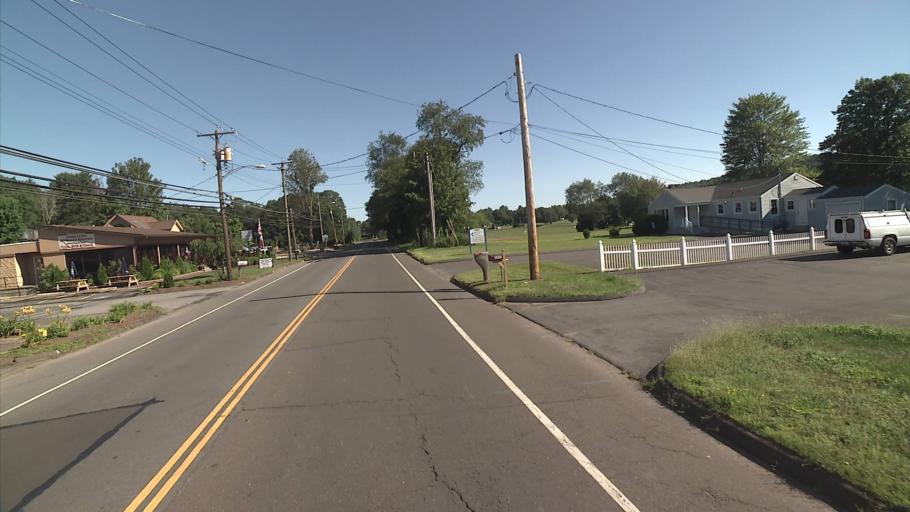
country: US
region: Connecticut
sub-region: New Haven County
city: Hamden
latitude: 41.4333
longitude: -72.9080
